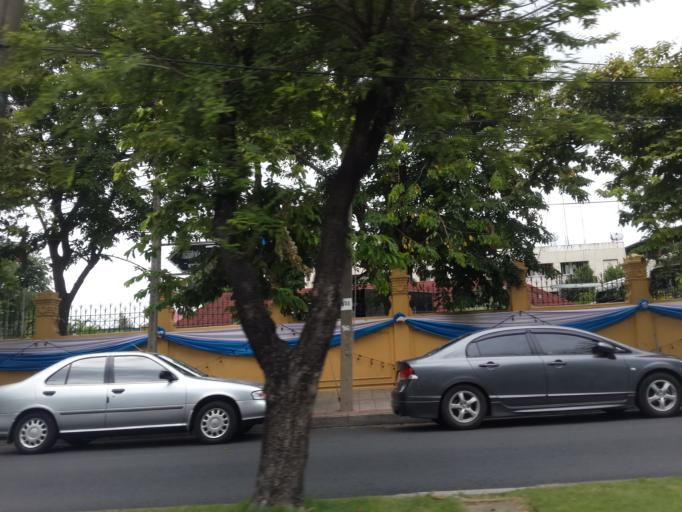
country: TH
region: Bangkok
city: Pom Prap Sattru Phai
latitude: 13.7686
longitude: 100.5105
